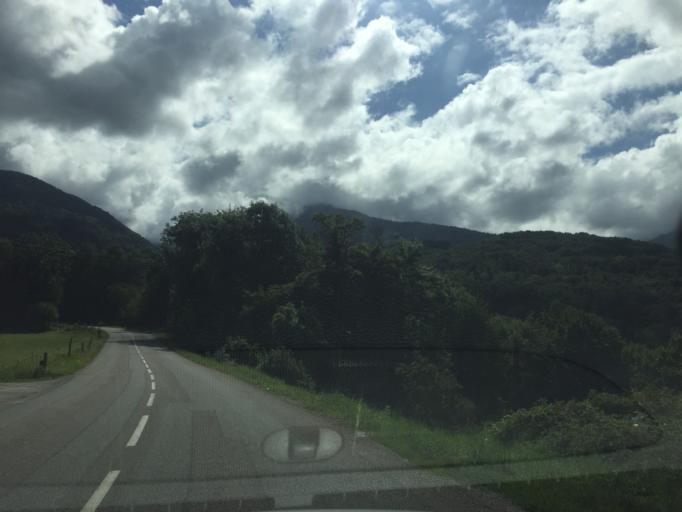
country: FR
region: Rhone-Alpes
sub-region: Departement de la Savoie
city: La Rochette
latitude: 45.4509
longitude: 6.1252
